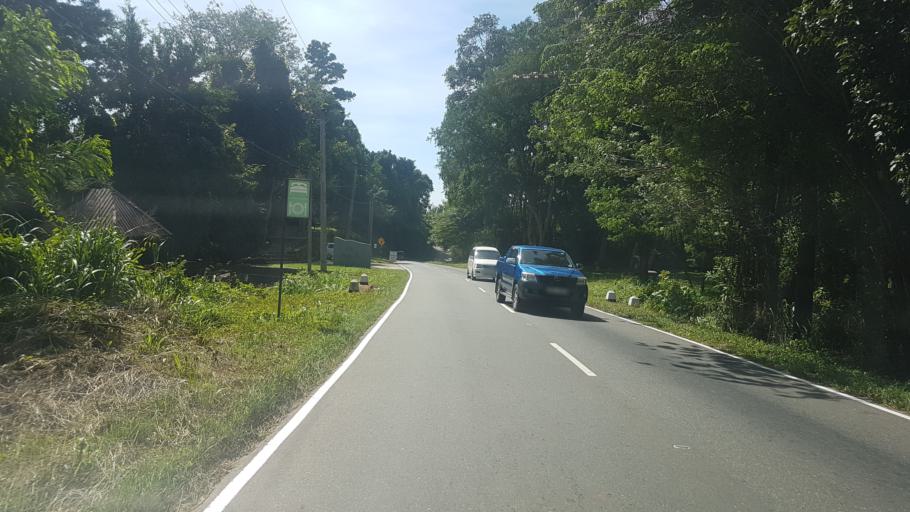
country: LK
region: Uva
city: Haputale
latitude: 6.8160
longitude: 81.0824
